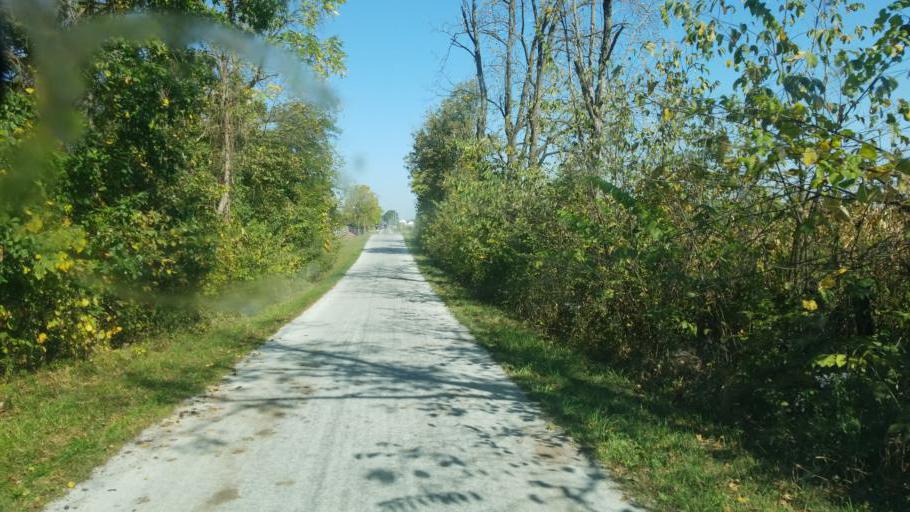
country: US
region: Ohio
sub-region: Hardin County
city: Kenton
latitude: 40.5590
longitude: -83.4862
